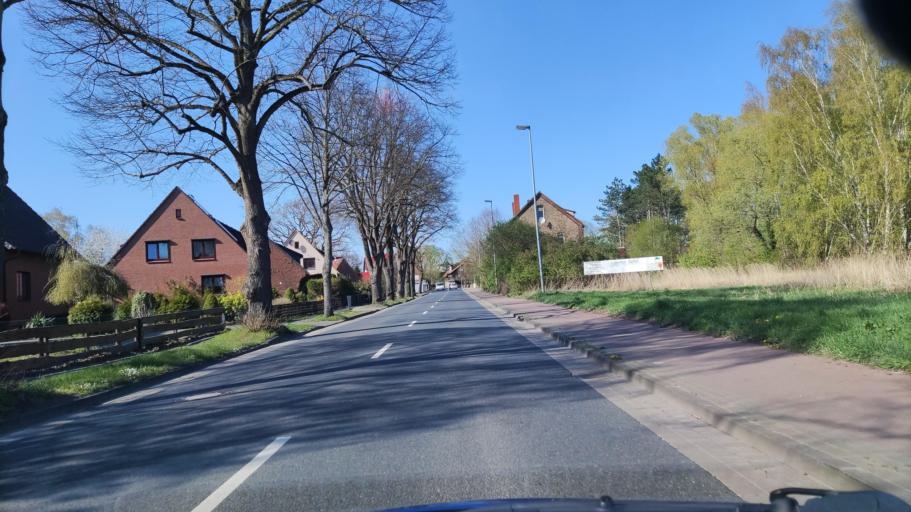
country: DE
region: Lower Saxony
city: Lehrte
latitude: 52.3661
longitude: 9.9764
